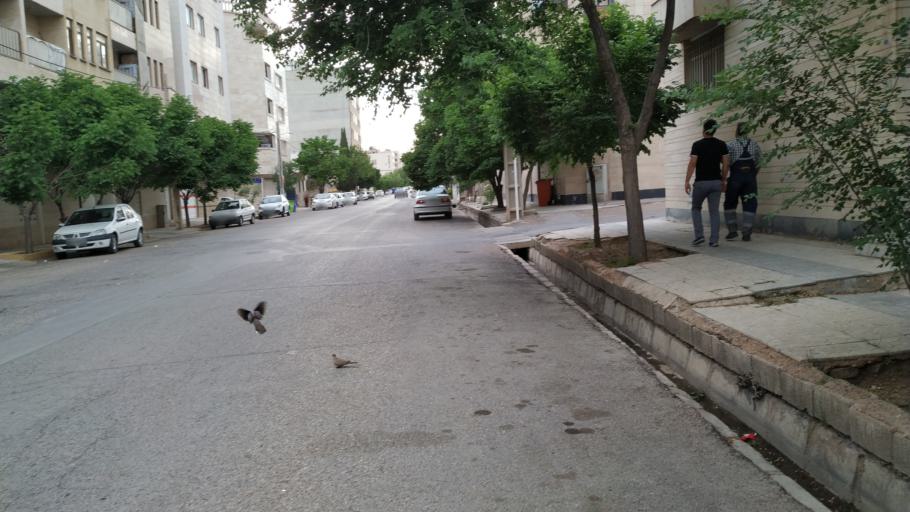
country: IR
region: Fars
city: Shiraz
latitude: 29.6086
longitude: 52.4885
